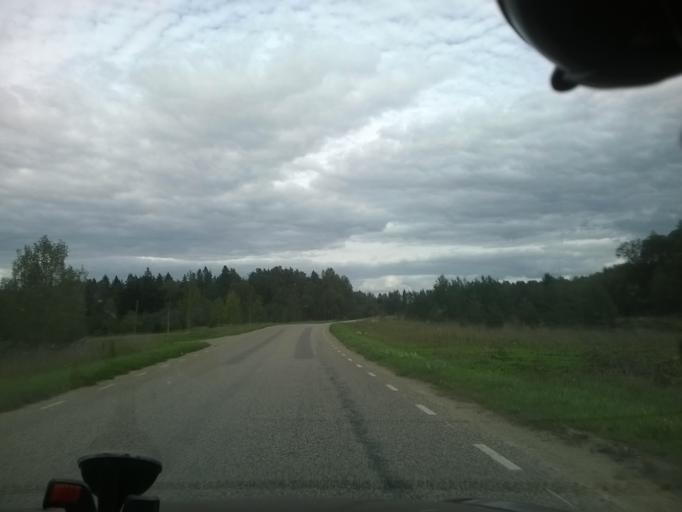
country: EE
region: Vorumaa
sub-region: Voru linn
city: Voru
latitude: 57.7516
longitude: 26.9756
